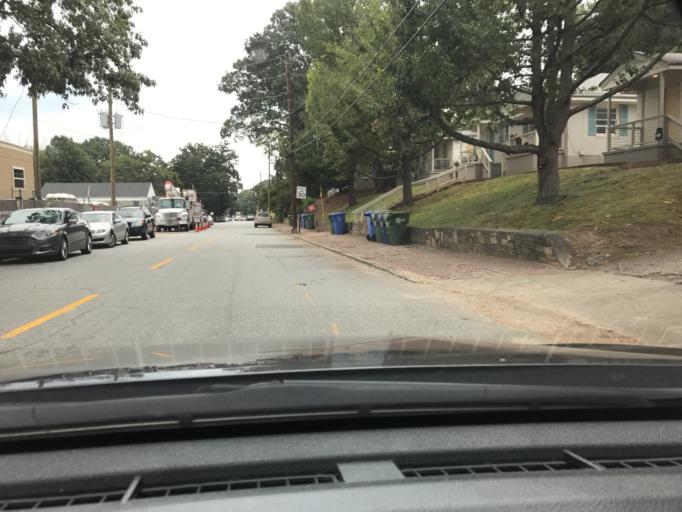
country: US
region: Georgia
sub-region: Fulton County
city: Atlanta
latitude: 33.7455
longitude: -84.3713
